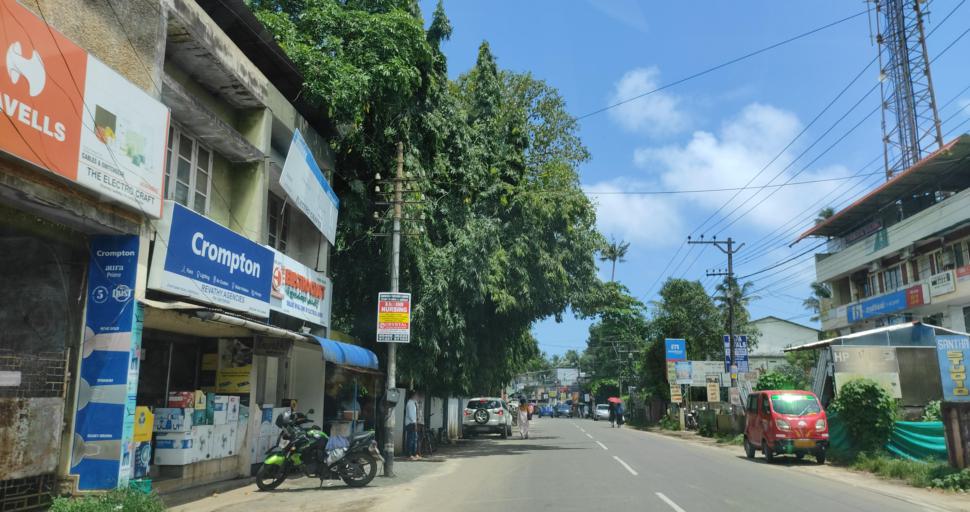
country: IN
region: Kerala
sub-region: Alappuzha
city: Shertallai
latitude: 9.6888
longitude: 76.3424
